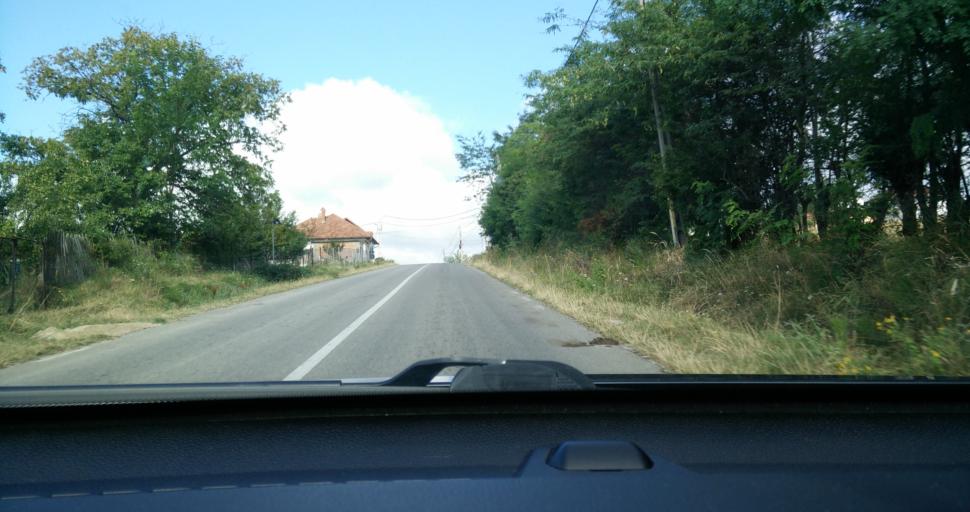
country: RO
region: Gorj
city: Novaci-Straini
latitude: 45.1798
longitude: 23.6947
